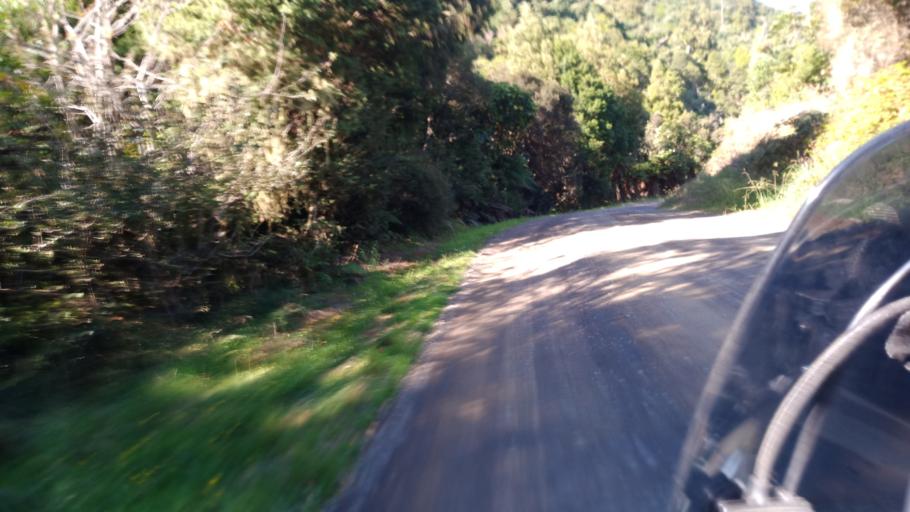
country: NZ
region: Bay of Plenty
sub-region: Opotiki District
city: Opotiki
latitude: -38.2471
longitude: 177.5925
